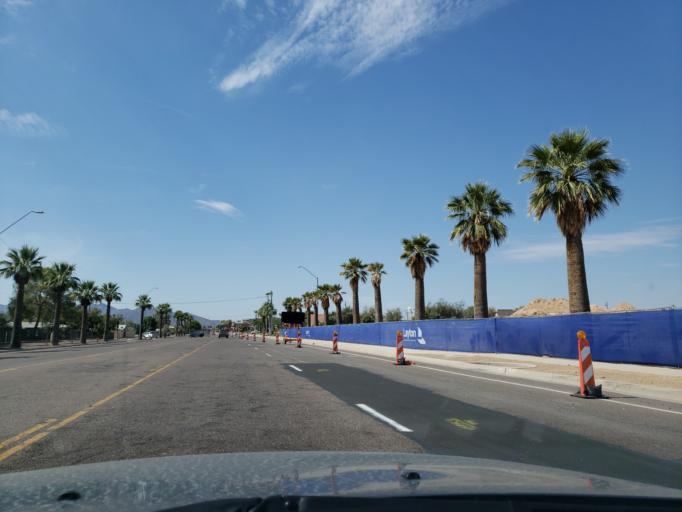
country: US
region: Arizona
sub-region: Maricopa County
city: Goodyear
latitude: 33.4403
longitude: -112.3584
